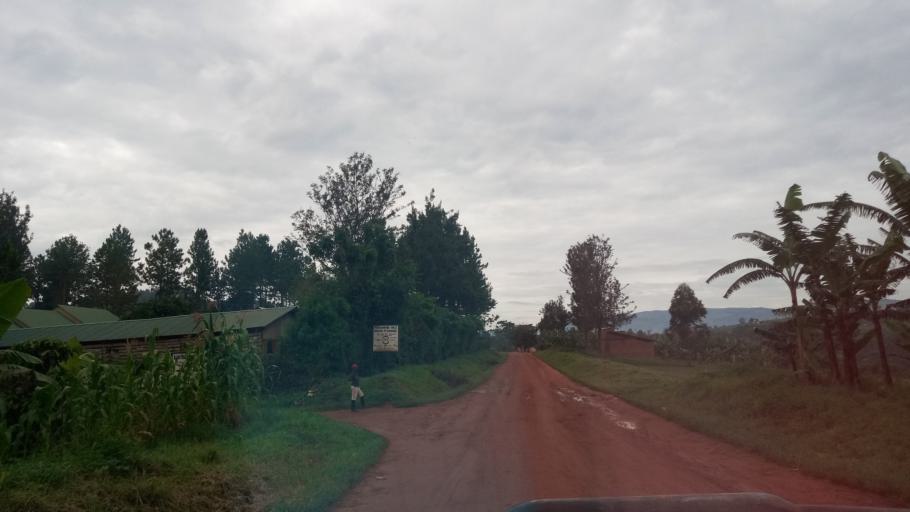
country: UG
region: Western Region
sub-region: Buhweju District
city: Buhweju
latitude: -0.1701
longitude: 30.4625
